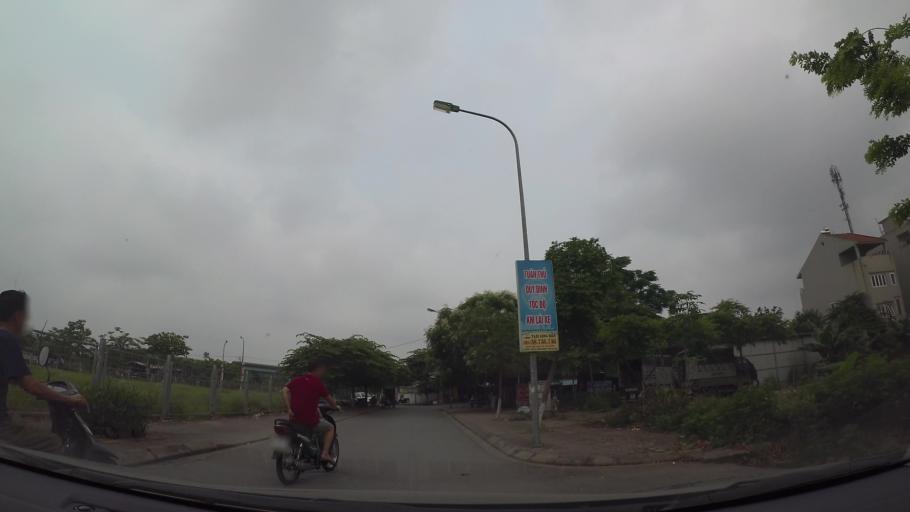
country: VN
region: Ha Noi
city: Trau Quy
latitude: 21.0426
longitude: 105.9265
